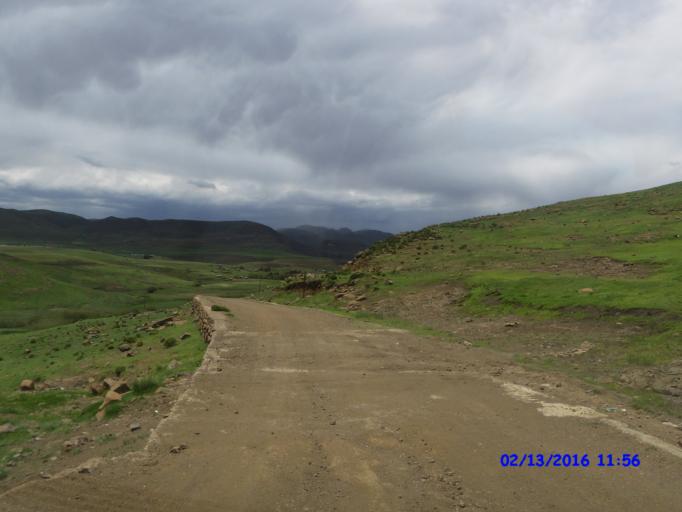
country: LS
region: Maseru
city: Nako
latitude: -29.8555
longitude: 28.0317
